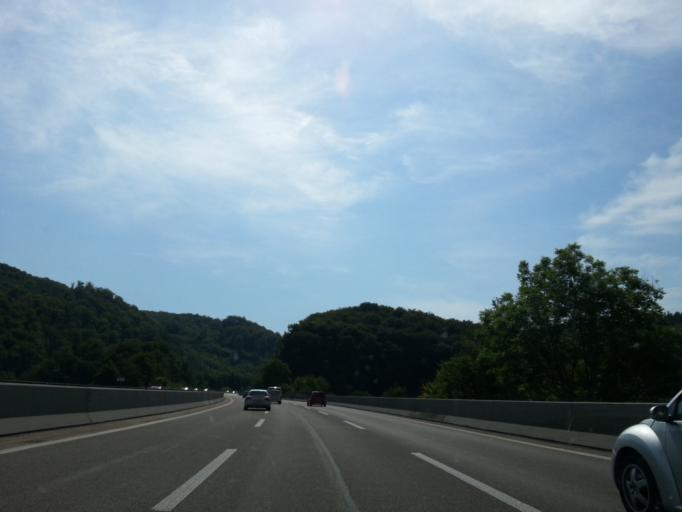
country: CH
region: Basel-Landschaft
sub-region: Bezirk Liestal
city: Arisdorf
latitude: 47.4976
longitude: 7.7650
